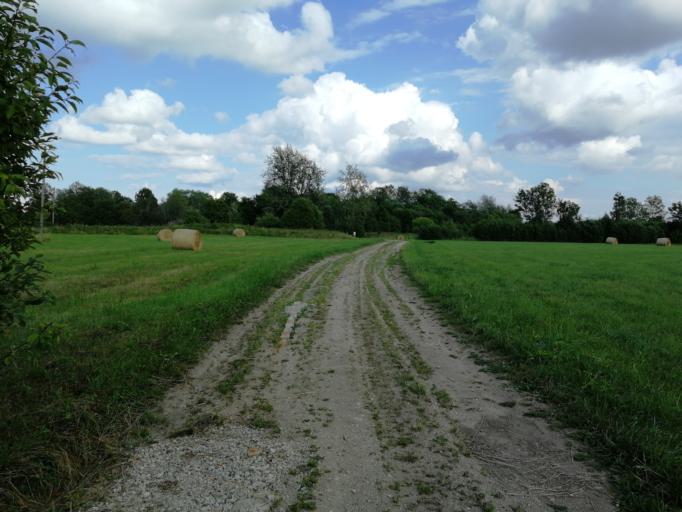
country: EE
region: Laeaene
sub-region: Lihula vald
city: Lihula
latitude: 58.7144
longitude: 23.8094
